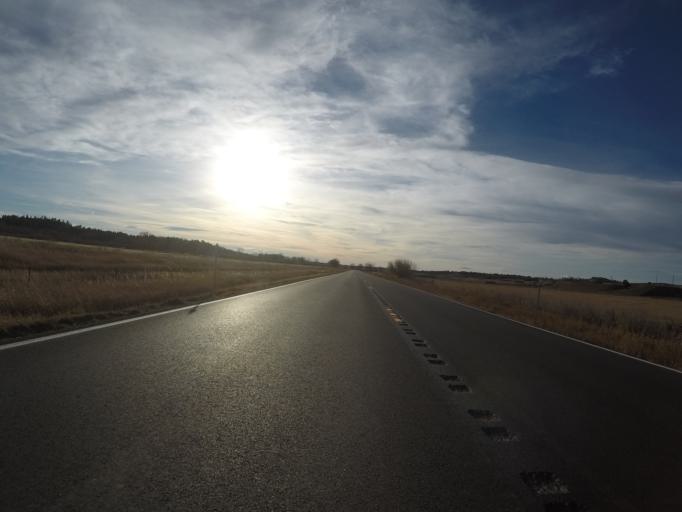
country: US
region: Montana
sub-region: Musselshell County
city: Roundup
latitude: 46.3642
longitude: -108.6561
